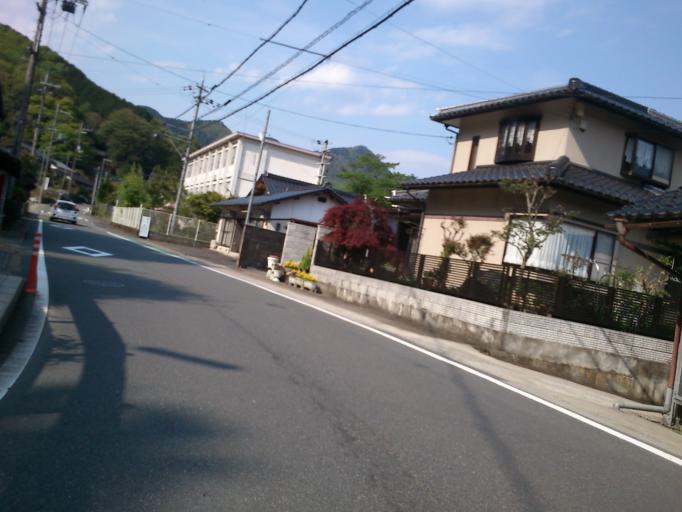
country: JP
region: Kyoto
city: Fukuchiyama
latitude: 35.3207
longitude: 135.0050
